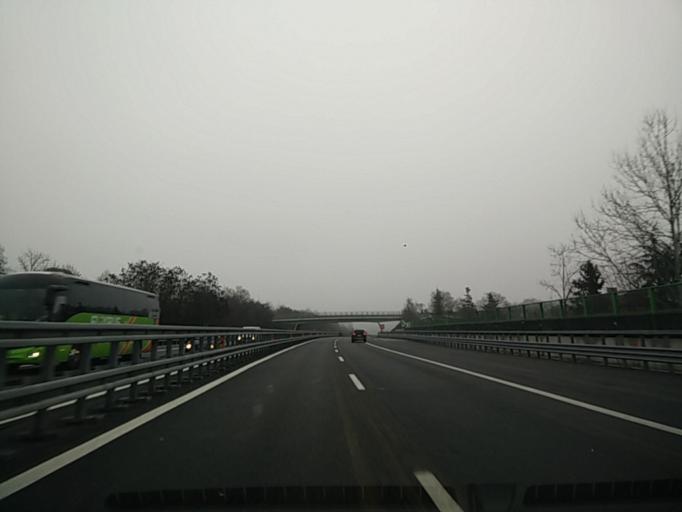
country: IT
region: Piedmont
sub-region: Provincia di Asti
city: Asti
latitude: 44.9177
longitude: 8.1989
